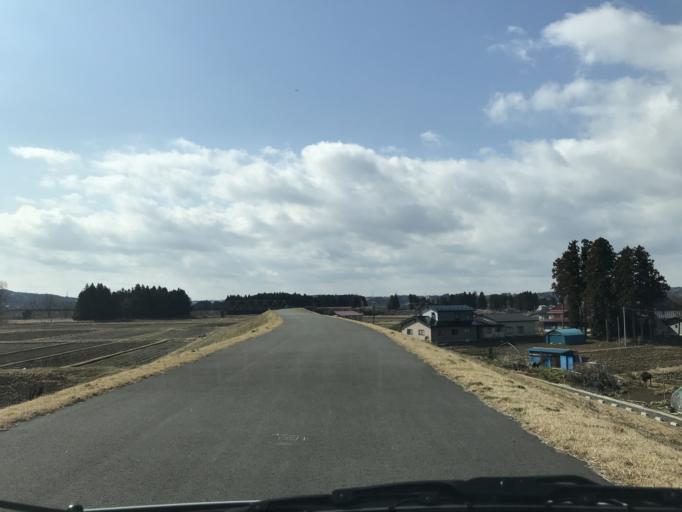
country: JP
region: Iwate
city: Mizusawa
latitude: 39.0460
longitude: 141.1469
